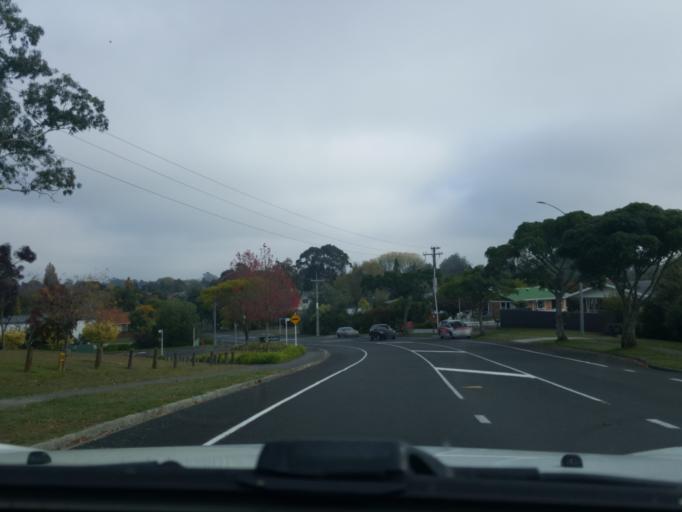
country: NZ
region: Waikato
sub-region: Hamilton City
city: Hamilton
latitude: -37.7542
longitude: 175.2901
